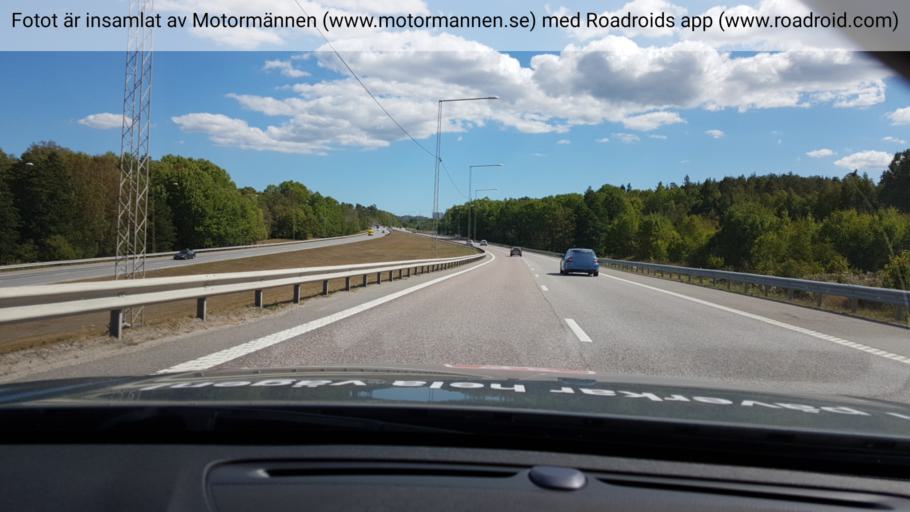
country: SE
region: Stockholm
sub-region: Nacka Kommun
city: Alta
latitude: 59.2639
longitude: 18.1461
